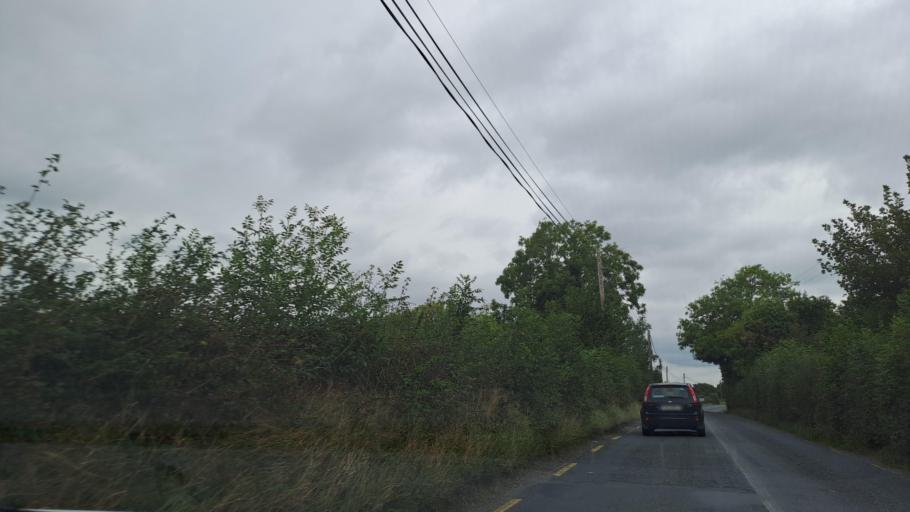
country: IE
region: Ulster
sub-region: An Cabhan
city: Bailieborough
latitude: 53.9810
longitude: -6.9120
